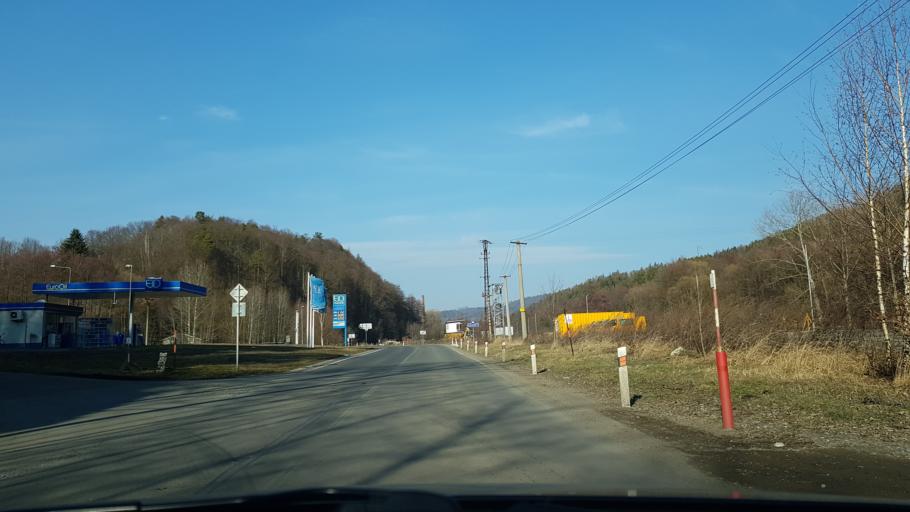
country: CZ
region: Olomoucky
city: Ruda nad Moravou
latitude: 49.9844
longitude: 16.8883
